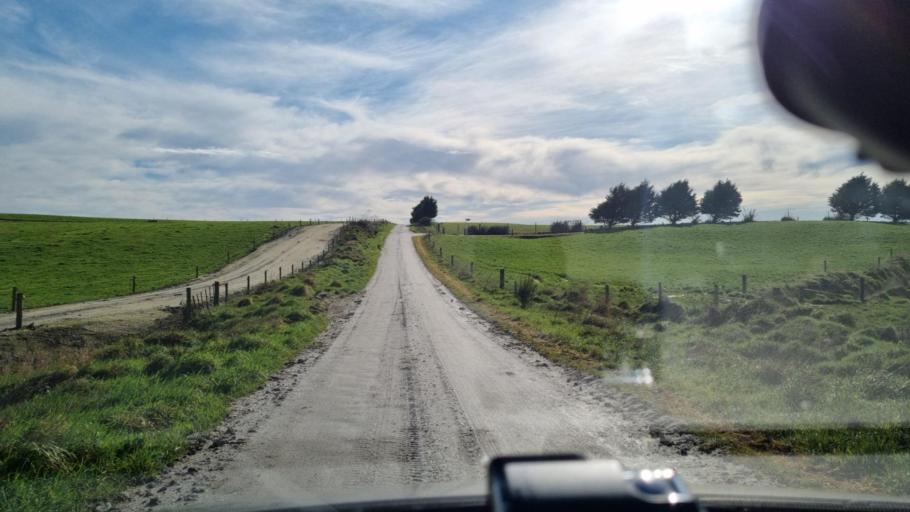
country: NZ
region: Southland
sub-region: Invercargill City
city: Invercargill
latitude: -46.4569
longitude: 168.4205
